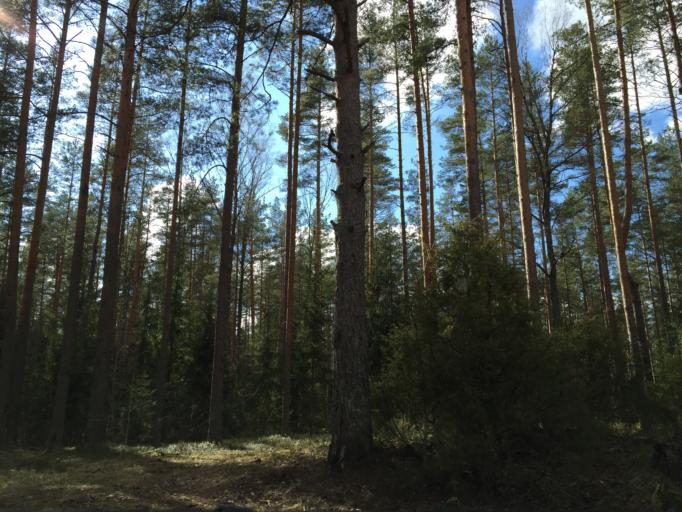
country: LV
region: Garkalne
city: Garkalne
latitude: 56.9537
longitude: 24.4677
